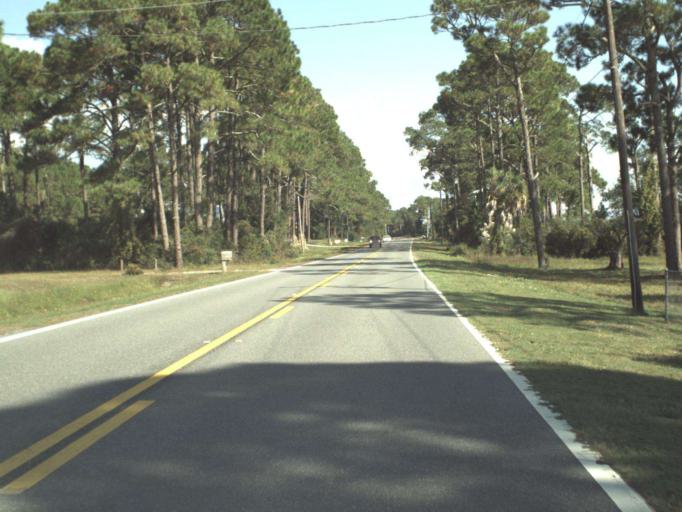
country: US
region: Florida
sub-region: Franklin County
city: Carrabelle
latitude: 29.9061
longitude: -84.5444
